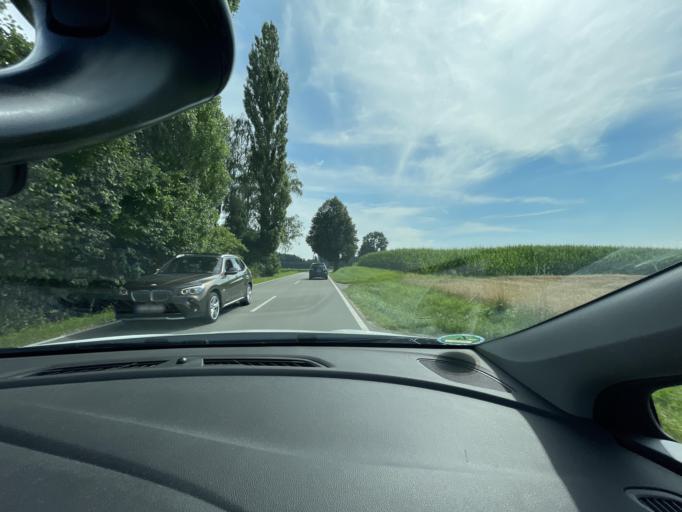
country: DE
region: Bavaria
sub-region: Upper Bavaria
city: Rohrmoos
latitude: 48.3161
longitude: 11.4098
